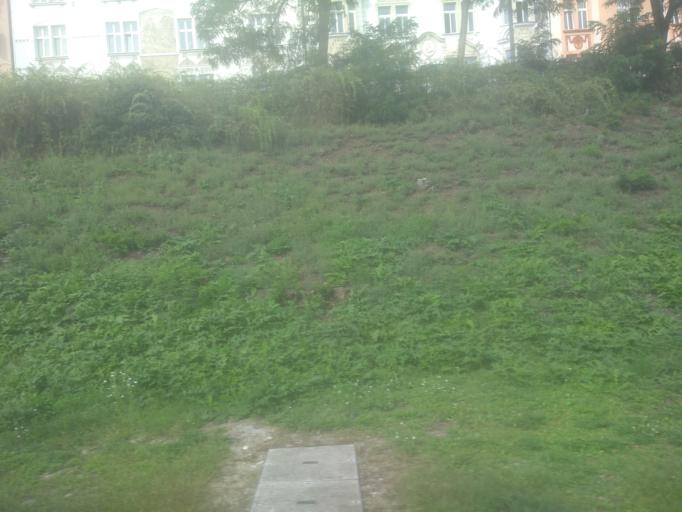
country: CZ
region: Plzensky
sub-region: Okres Plzen-Mesto
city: Pilsen
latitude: 49.7407
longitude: 13.3662
